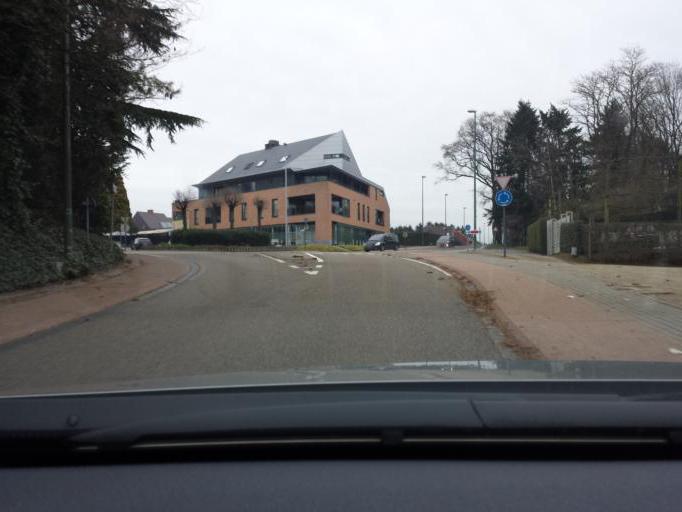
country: BE
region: Flanders
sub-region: Provincie Limburg
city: Lummen
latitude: 50.9911
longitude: 5.1944
